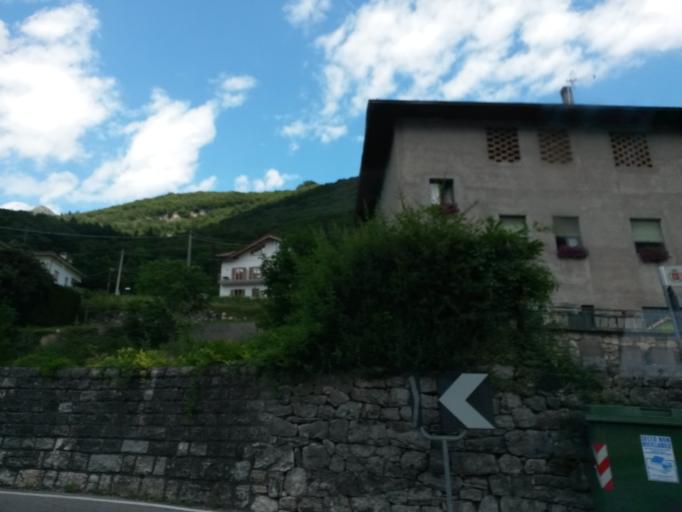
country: IT
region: Trentino-Alto Adige
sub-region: Provincia di Trento
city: Tenno
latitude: 45.9209
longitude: 10.8315
